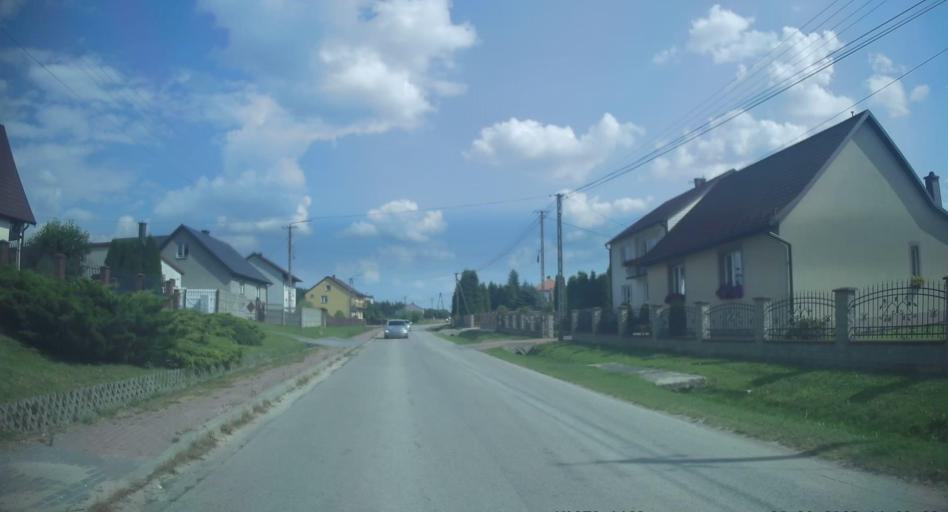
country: PL
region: Swietokrzyskie
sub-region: Powiat kielecki
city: Checiny
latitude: 50.8160
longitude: 20.4031
